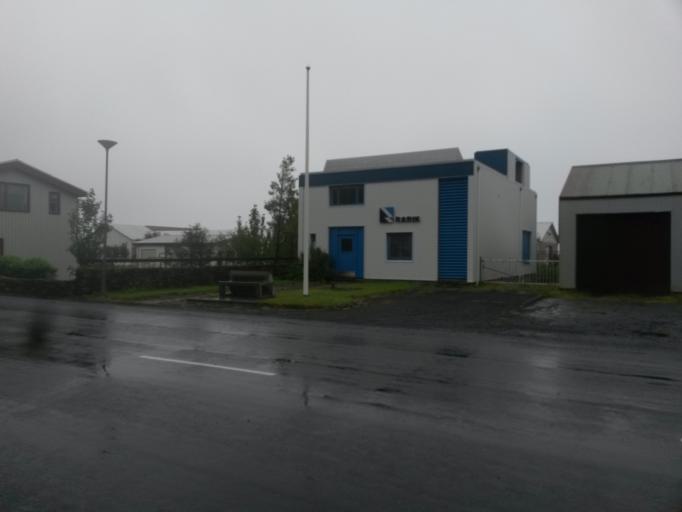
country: IS
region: South
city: Vestmannaeyjar
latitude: 63.4178
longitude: -19.0132
